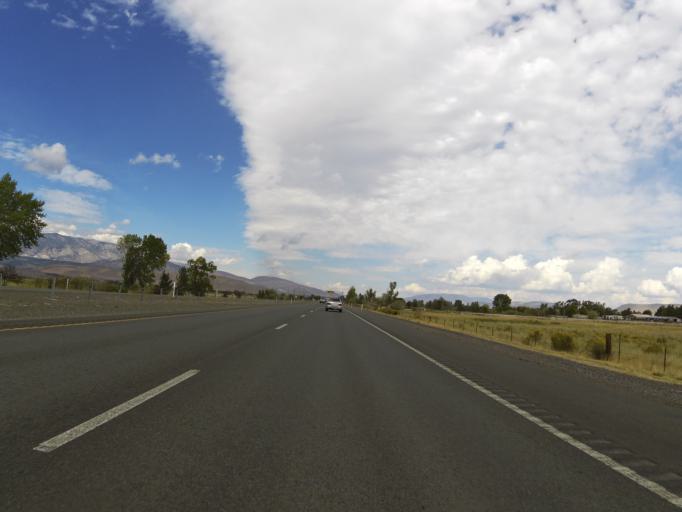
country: US
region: Nevada
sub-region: Douglas County
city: Johnson Lane
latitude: 39.0215
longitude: -119.7796
